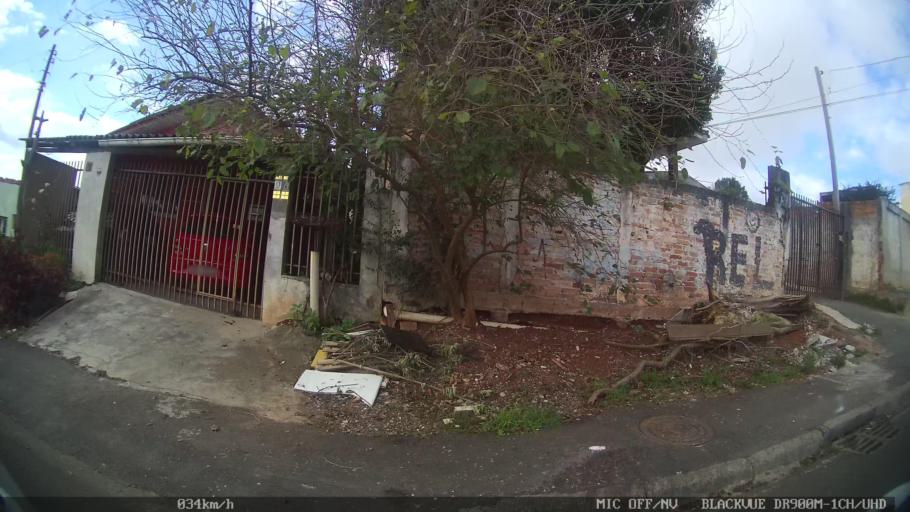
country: BR
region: Parana
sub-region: Colombo
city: Colombo
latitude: -25.3549
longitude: -49.1936
